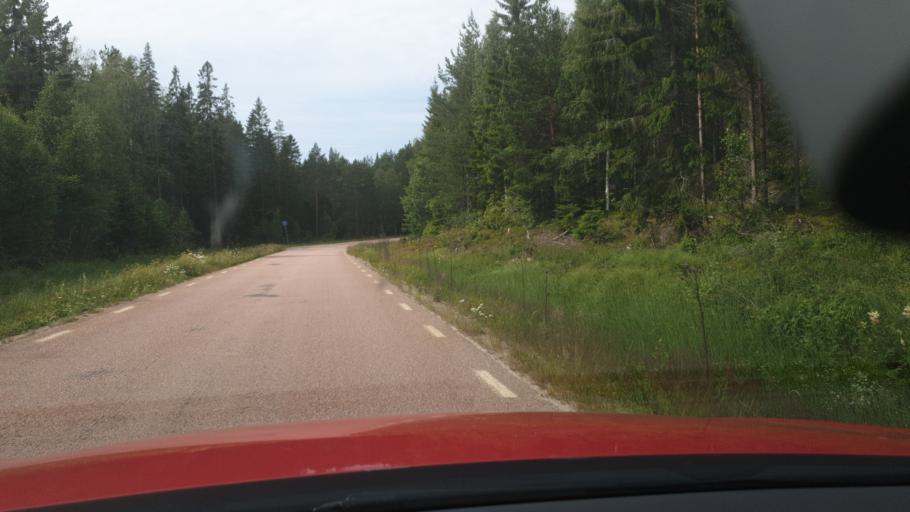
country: SE
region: Gaevleborg
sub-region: Hudiksvalls Kommun
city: Hudiksvall
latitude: 61.6995
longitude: 17.4646
